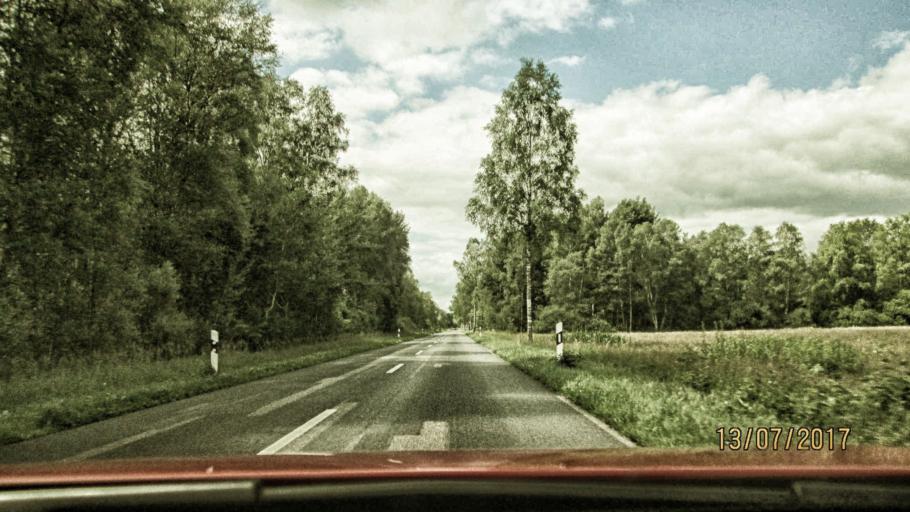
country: DE
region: Lower Saxony
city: Sassenburg
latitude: 52.5651
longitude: 10.6276
